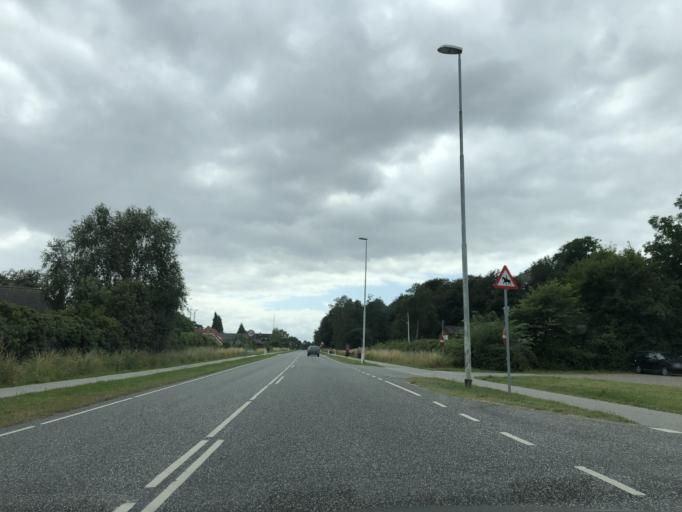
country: DK
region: South Denmark
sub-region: Sonderborg Kommune
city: Guderup
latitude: 54.9928
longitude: 9.9819
